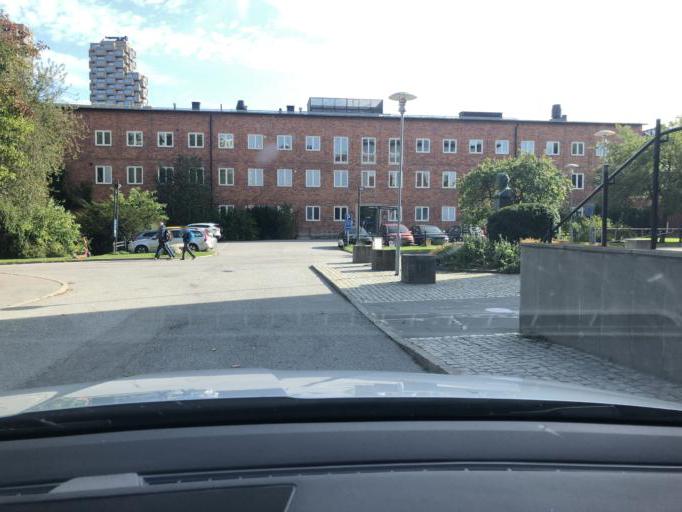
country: SE
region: Stockholm
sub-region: Solna Kommun
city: Solna
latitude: 59.3477
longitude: 18.0281
